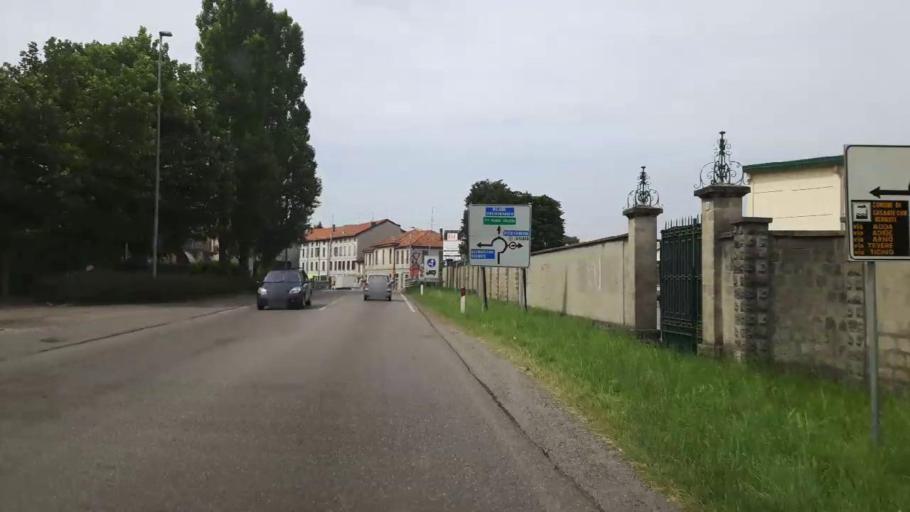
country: IT
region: Lombardy
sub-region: Provincia di Como
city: Grandate
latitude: 45.7611
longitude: 9.0531
